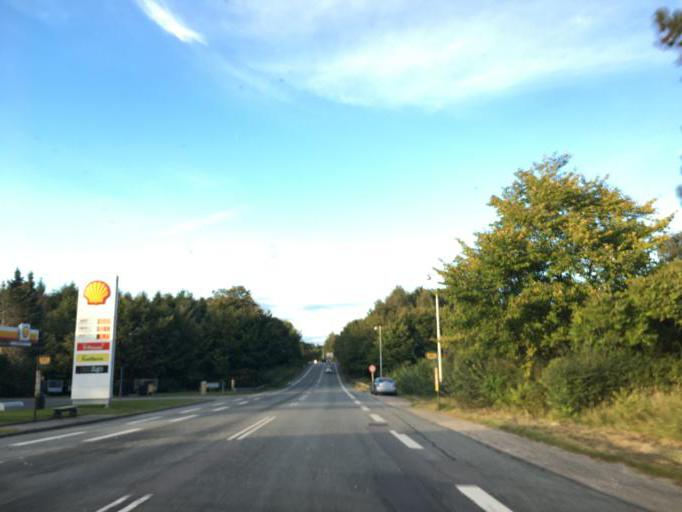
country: DK
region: Capital Region
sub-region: Horsholm Kommune
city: Horsholm
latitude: 55.8640
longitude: 12.4967
